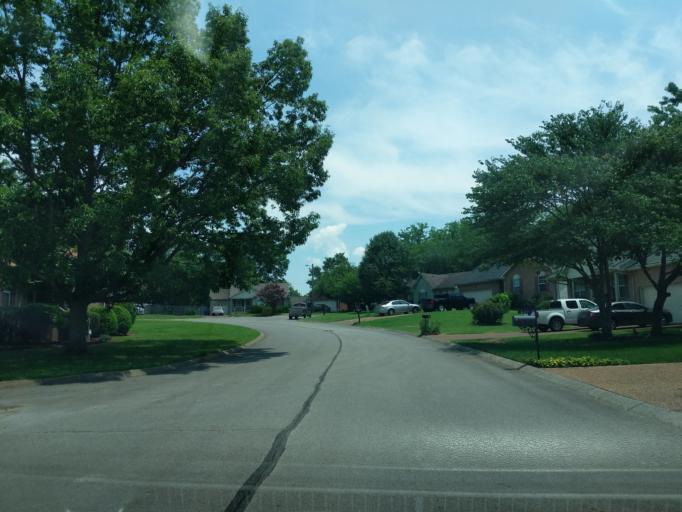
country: US
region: Tennessee
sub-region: Davidson County
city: Lakewood
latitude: 36.2374
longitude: -86.6394
